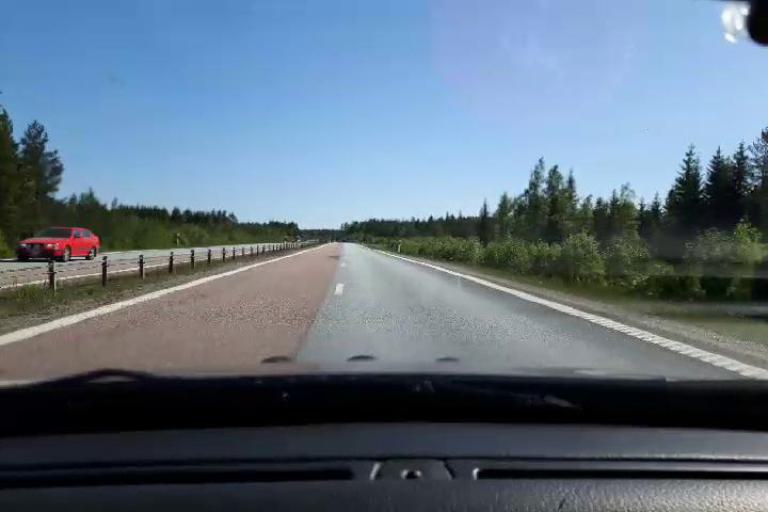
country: SE
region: Gaevleborg
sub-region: Soderhamns Kommun
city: Soderhamn
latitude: 61.4243
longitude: 16.9842
